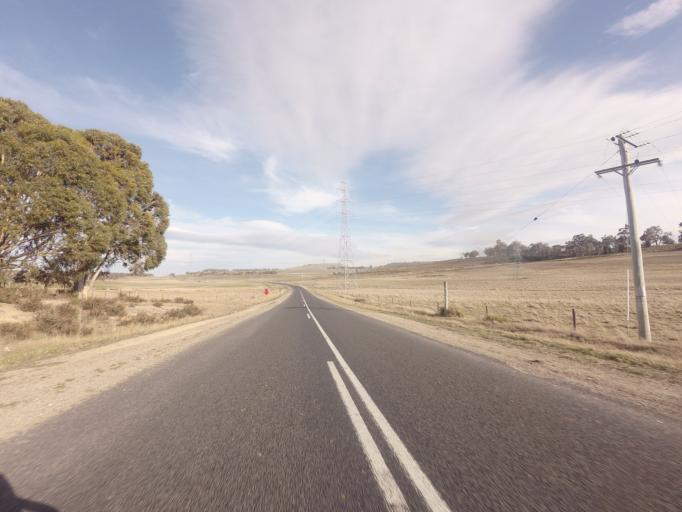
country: AU
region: Tasmania
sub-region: Derwent Valley
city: New Norfolk
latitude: -42.2598
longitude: 146.9377
